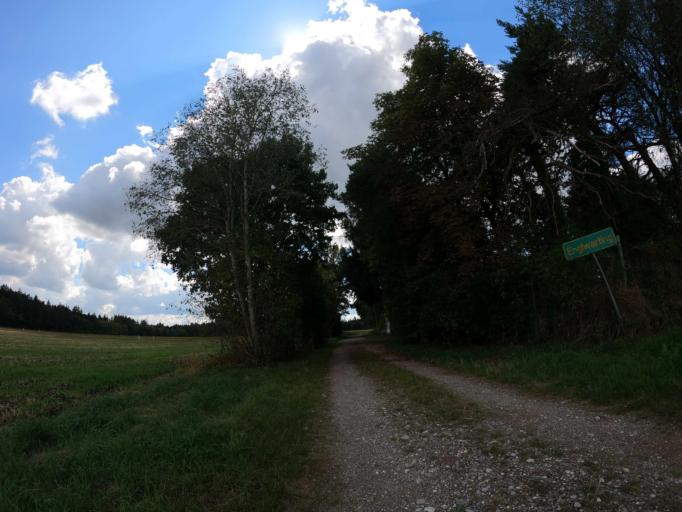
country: DE
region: Bavaria
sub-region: Upper Bavaria
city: Brunnthal
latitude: 48.0185
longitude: 11.6678
